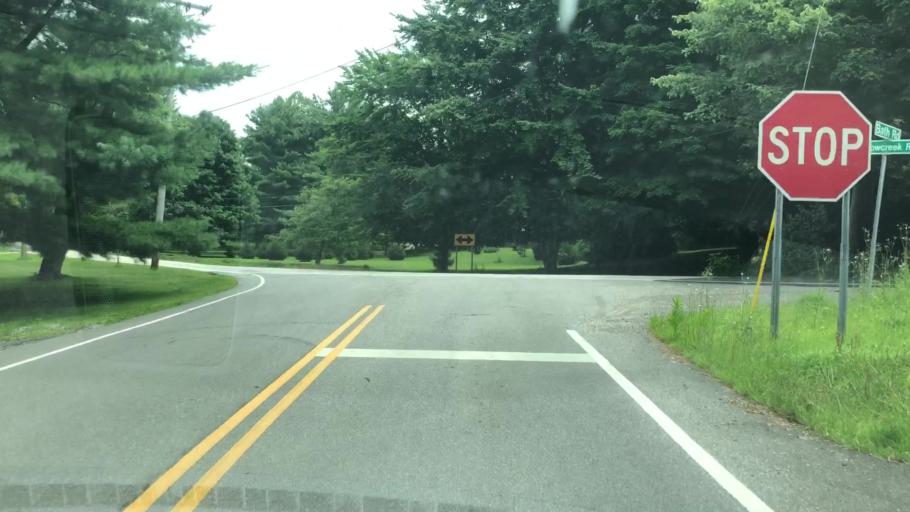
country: US
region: Ohio
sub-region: Summit County
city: Fairlawn
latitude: 41.1622
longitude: -81.5816
